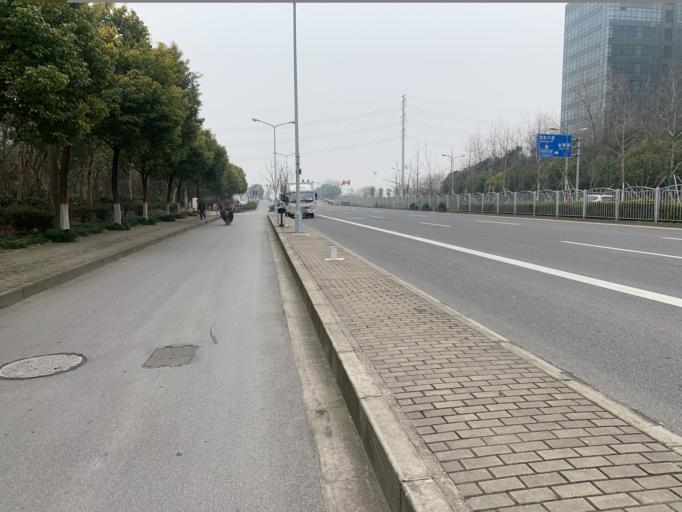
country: CN
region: Shanghai Shi
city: Huamu
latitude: 31.2459
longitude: 121.6212
